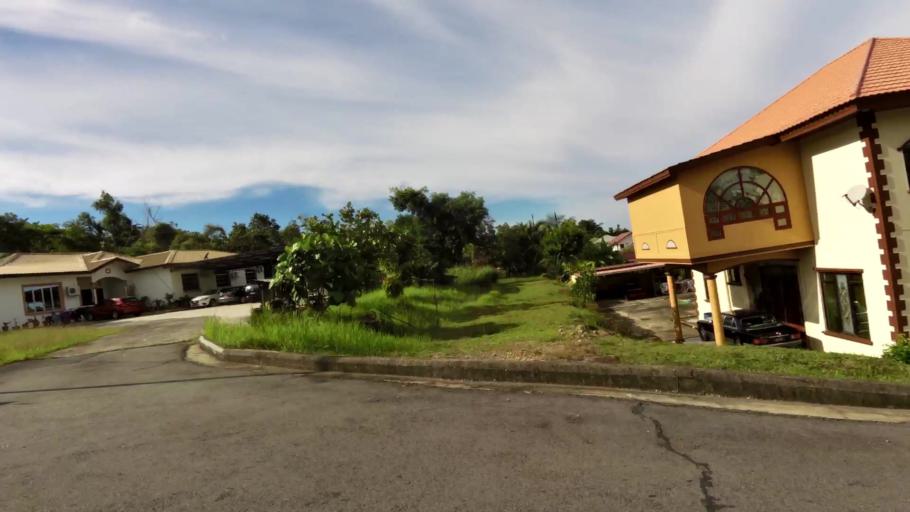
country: BN
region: Brunei and Muara
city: Bandar Seri Begawan
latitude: 4.9802
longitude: 115.0202
